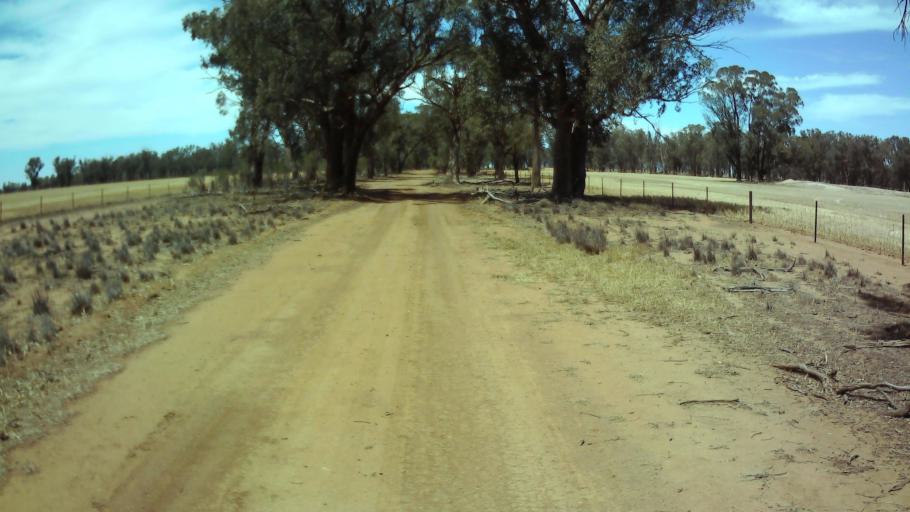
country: AU
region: New South Wales
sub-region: Weddin
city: Grenfell
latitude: -33.9073
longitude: 147.8071
